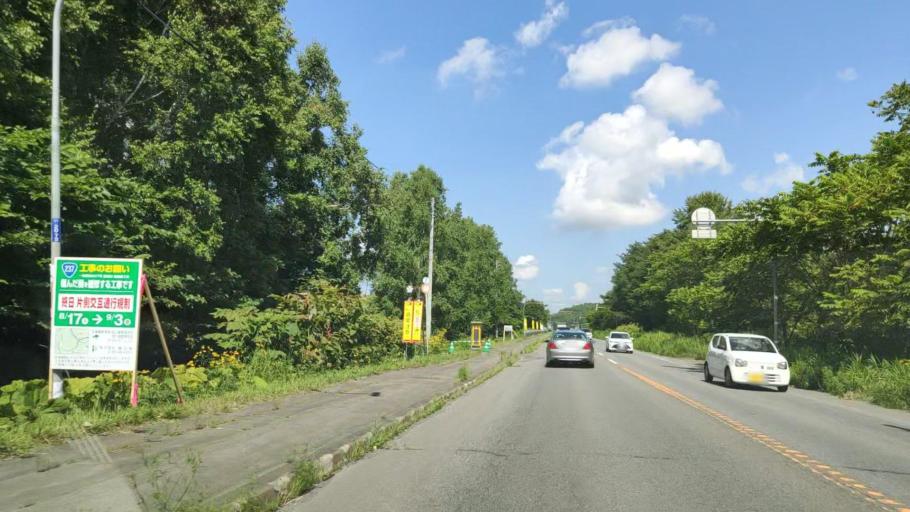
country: JP
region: Hokkaido
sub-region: Asahikawa-shi
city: Asahikawa
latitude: 43.6224
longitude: 142.4685
